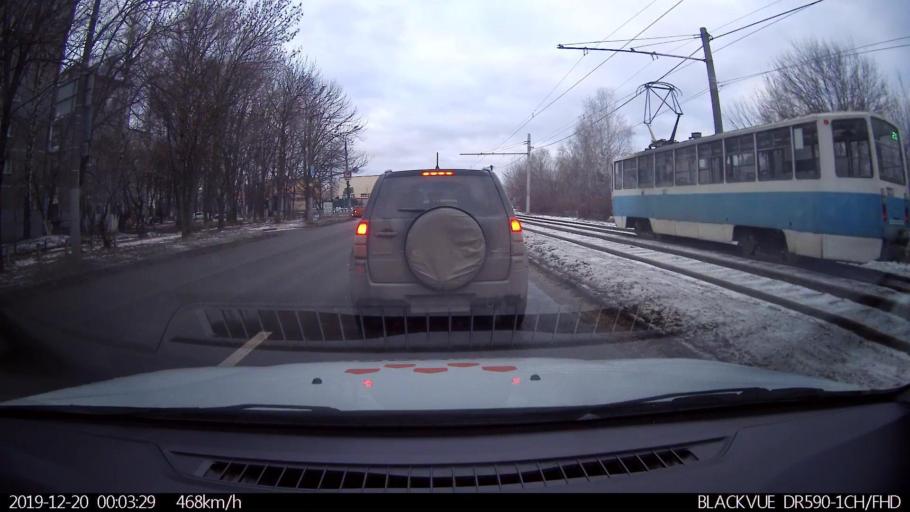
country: RU
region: Jaroslavl
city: Tutayev
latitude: 58.0755
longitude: 39.6886
